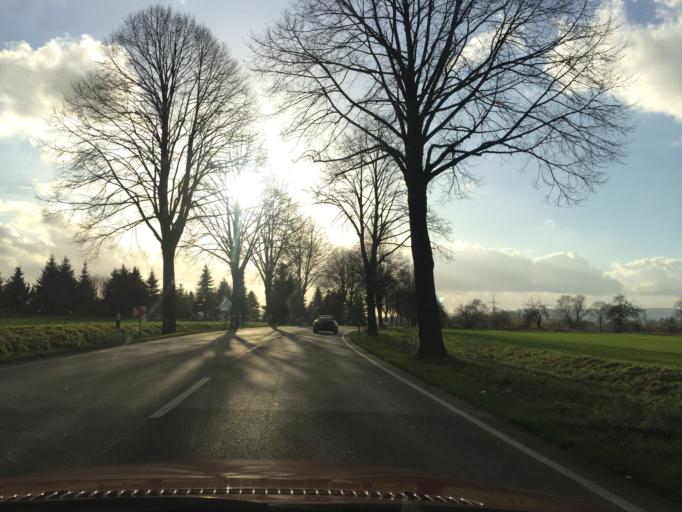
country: DE
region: Lower Saxony
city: Bevern
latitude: 51.8502
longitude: 9.4875
